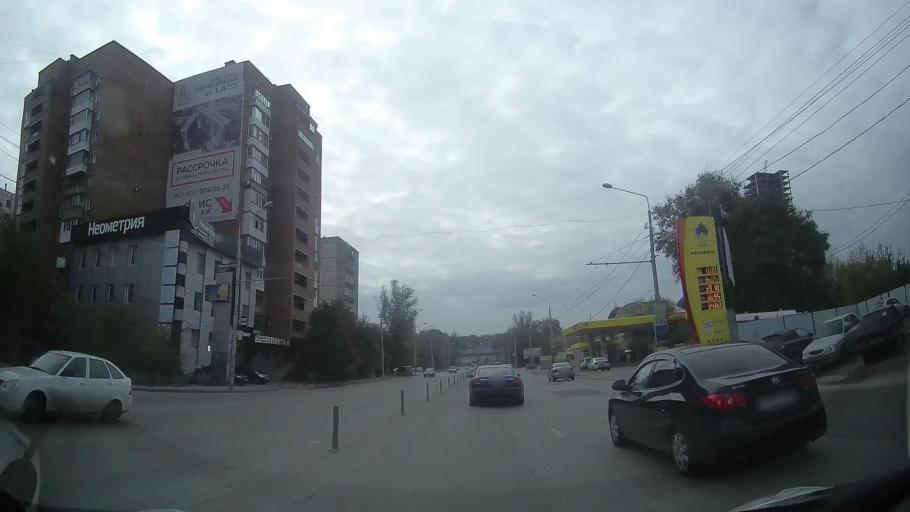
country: RU
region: Rostov
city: Rostov-na-Donu
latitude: 47.2483
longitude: 39.6970
